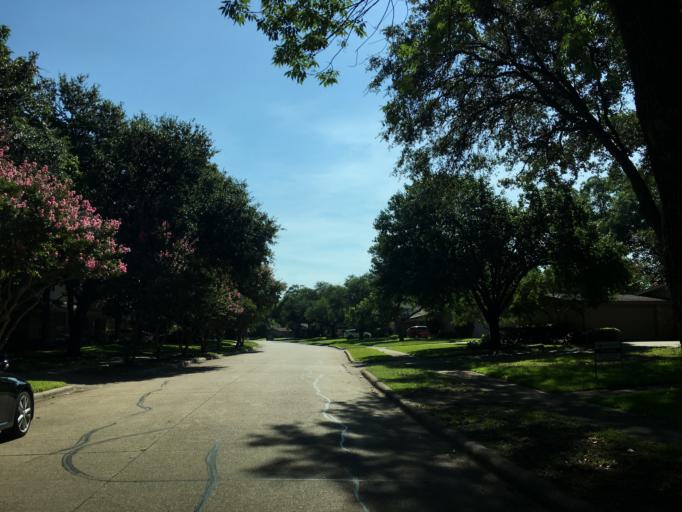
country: US
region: Texas
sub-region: Dallas County
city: Farmers Branch
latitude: 32.9179
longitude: -96.8718
